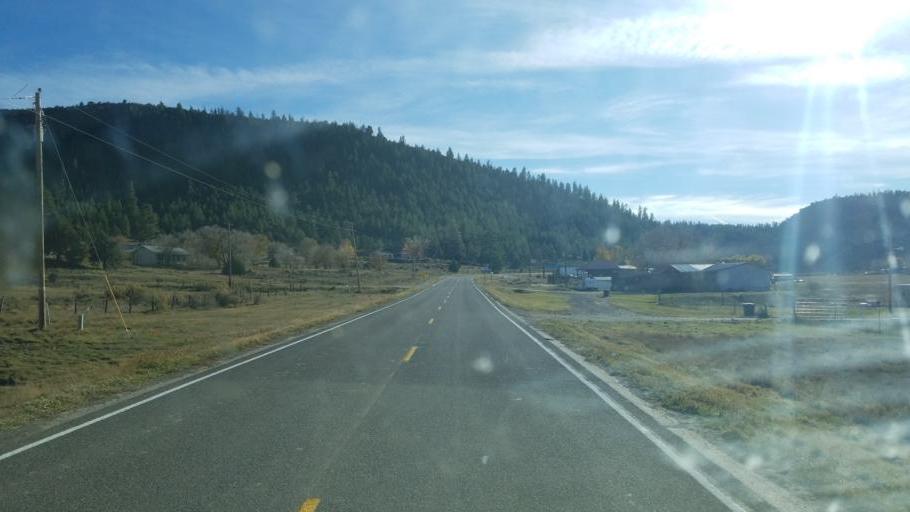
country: US
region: New Mexico
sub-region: Rio Arriba County
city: Dulce
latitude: 36.9161
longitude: -106.9941
